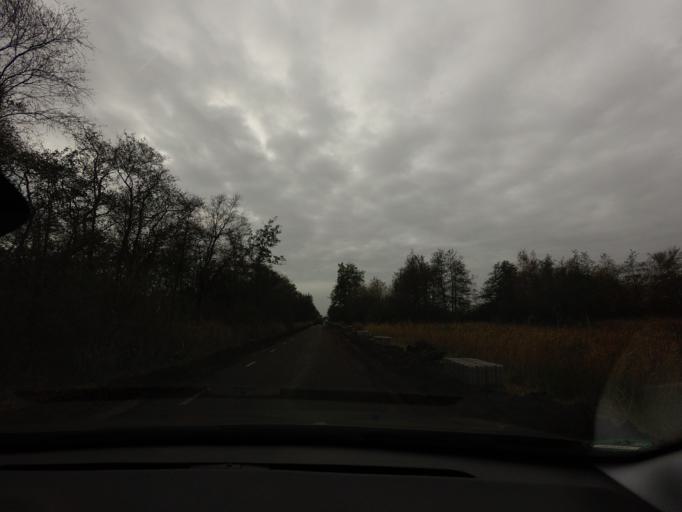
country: NL
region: Overijssel
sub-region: Gemeente Steenwijkerland
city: Oldemarkt
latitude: 52.7771
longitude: 5.9734
